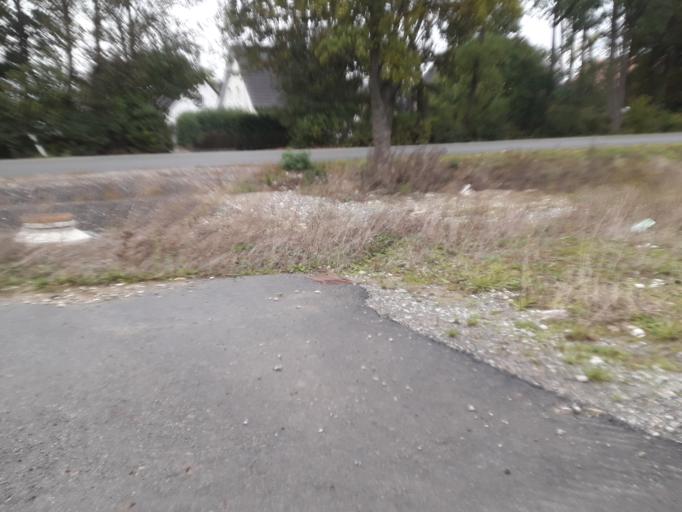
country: DE
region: North Rhine-Westphalia
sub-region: Regierungsbezirk Detmold
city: Paderborn
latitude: 51.7183
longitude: 8.8061
